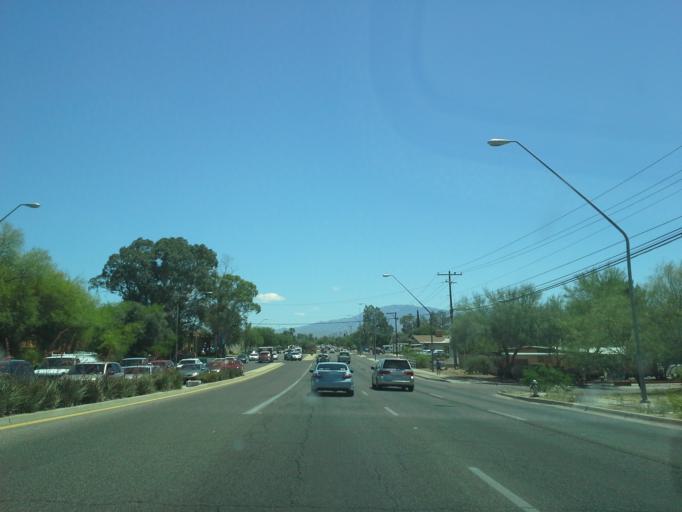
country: US
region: Arizona
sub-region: Pima County
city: Tucson
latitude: 32.2506
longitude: -110.8630
